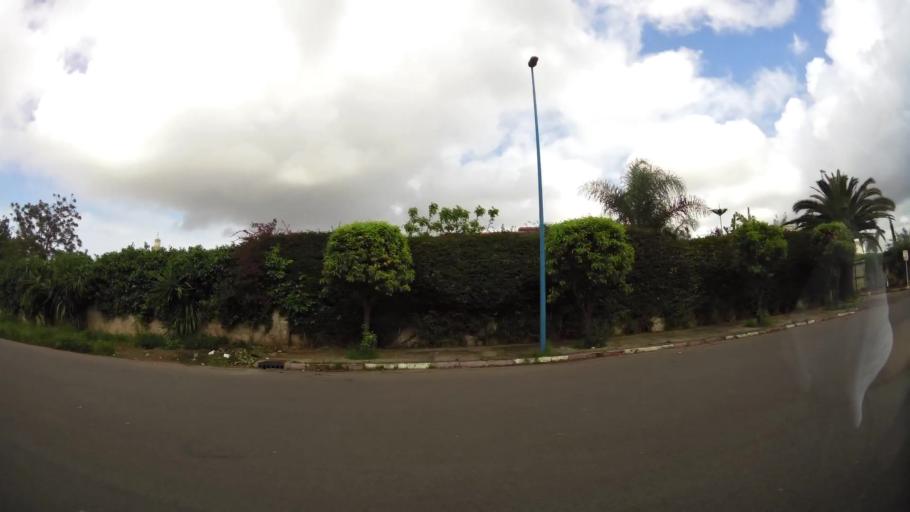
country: MA
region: Grand Casablanca
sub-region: Casablanca
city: Casablanca
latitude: 33.5494
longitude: -7.6158
